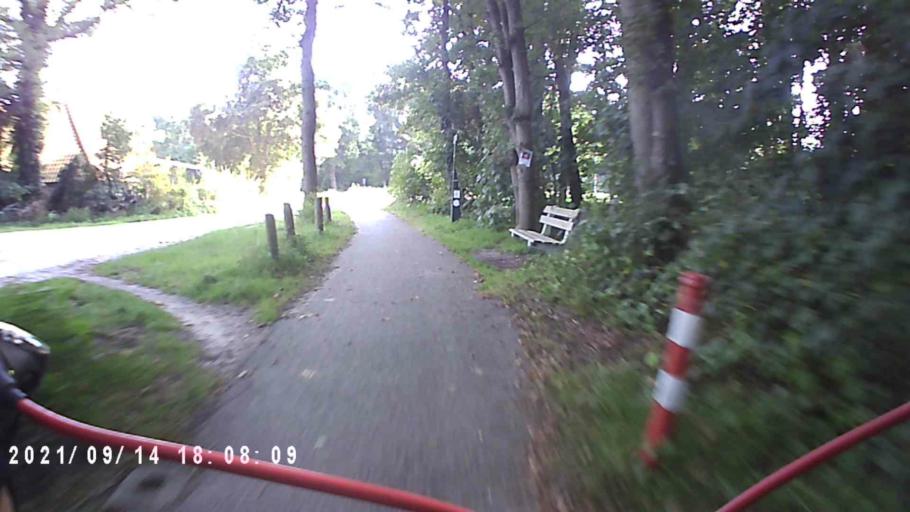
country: NL
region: Drenthe
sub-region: Gemeente Tynaarlo
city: Zuidlaren
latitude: 53.1018
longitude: 6.6570
